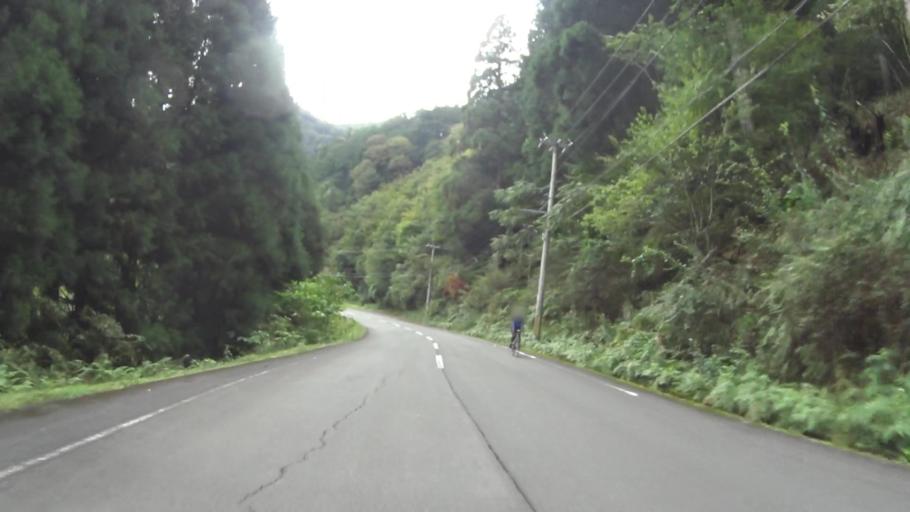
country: JP
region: Fukui
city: Obama
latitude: 35.3174
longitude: 135.6507
